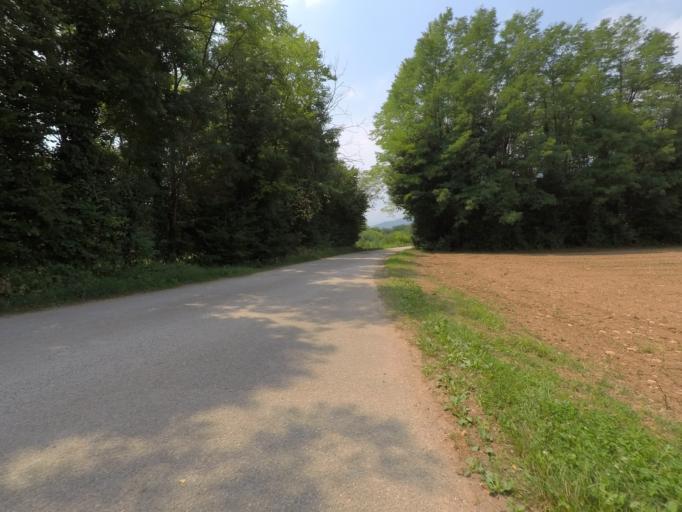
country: IT
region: Friuli Venezia Giulia
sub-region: Provincia di Pordenone
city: Marsure
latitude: 46.1065
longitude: 12.6189
